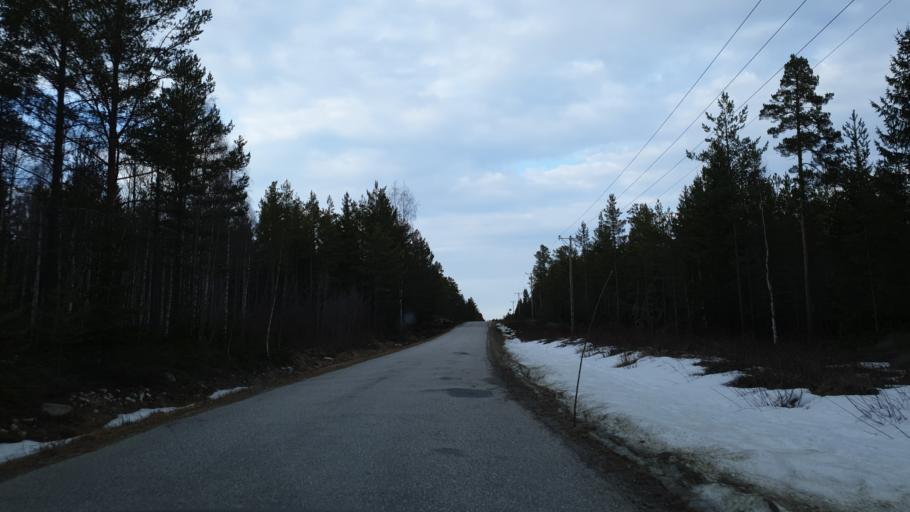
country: SE
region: Vaesternorrland
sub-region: Sundsvalls Kommun
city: Njurundabommen
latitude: 61.9898
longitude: 17.3772
